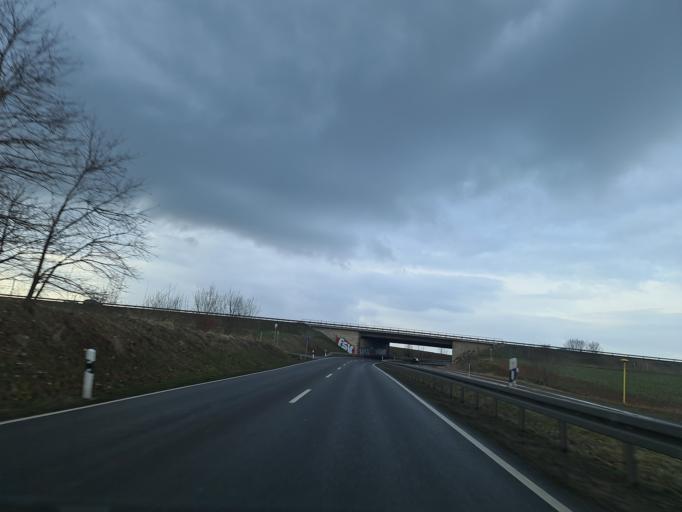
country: DE
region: Saxony
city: Reinsdorf
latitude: 50.6827
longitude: 12.5907
